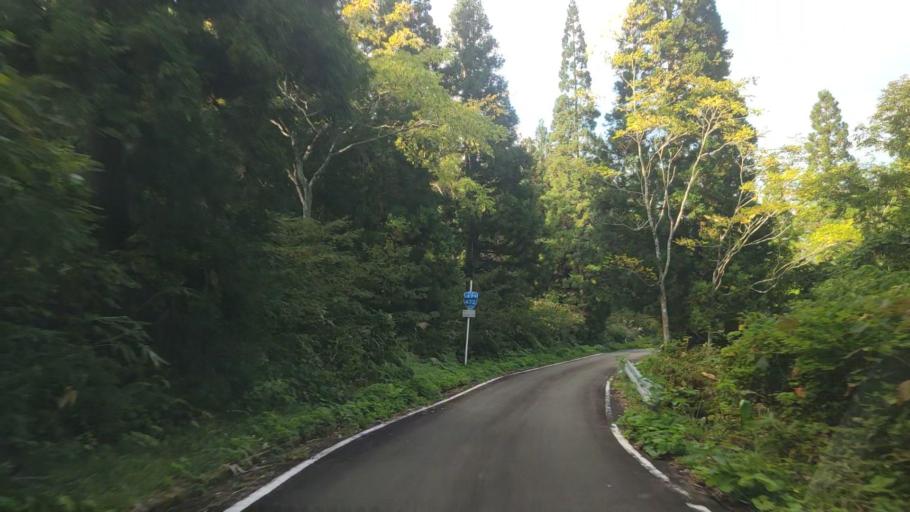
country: JP
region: Toyama
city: Yatsuomachi-higashikumisaka
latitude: 36.3681
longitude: 137.0758
